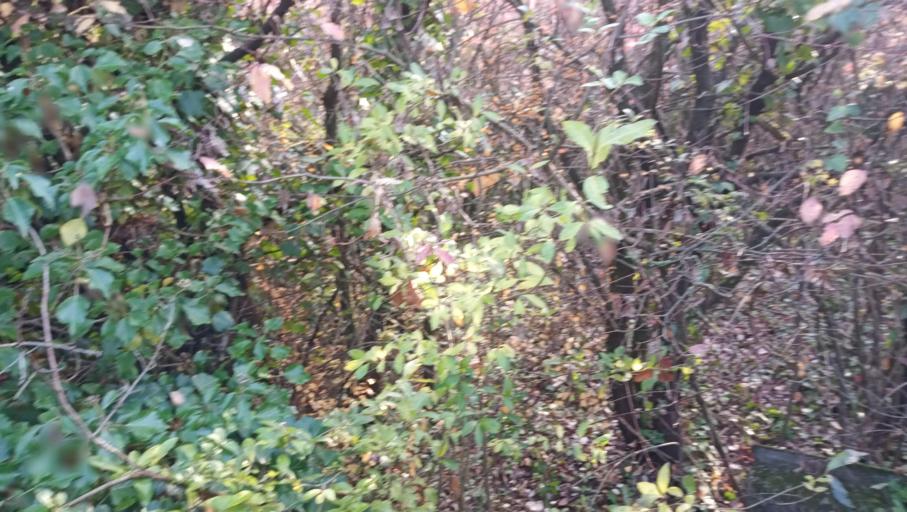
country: HU
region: Pest
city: Urom
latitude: 47.5922
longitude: 19.0329
